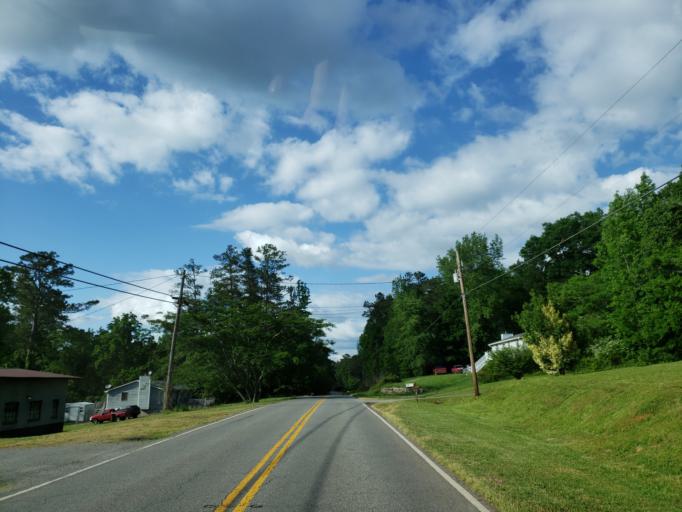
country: US
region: Georgia
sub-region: Bartow County
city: Cartersville
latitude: 34.2355
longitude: -84.8543
